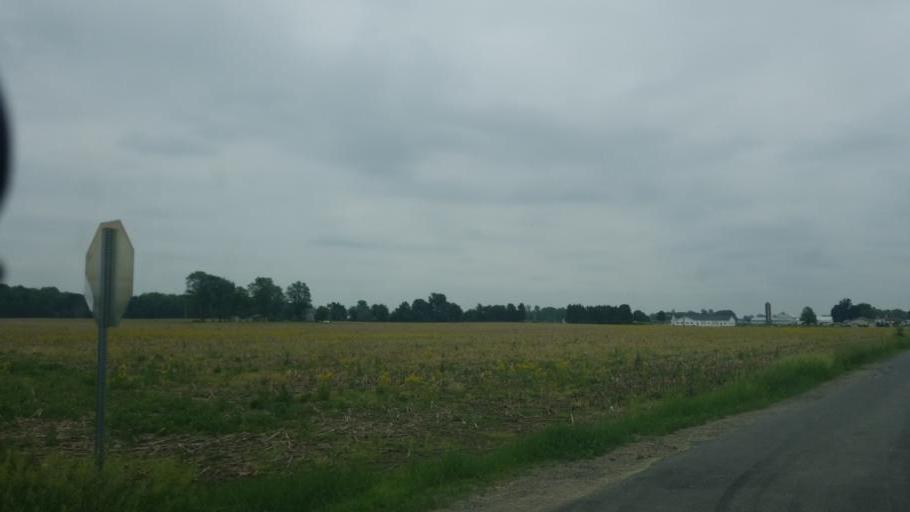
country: US
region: Indiana
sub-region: Elkhart County
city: Wakarusa
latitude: 41.4934
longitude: -86.0594
